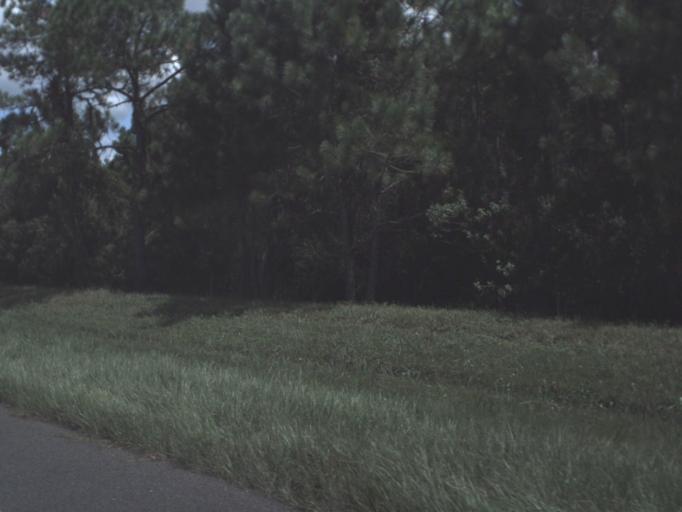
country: US
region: Florida
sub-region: Pasco County
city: Wesley Chapel
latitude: 28.2137
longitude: -82.3532
